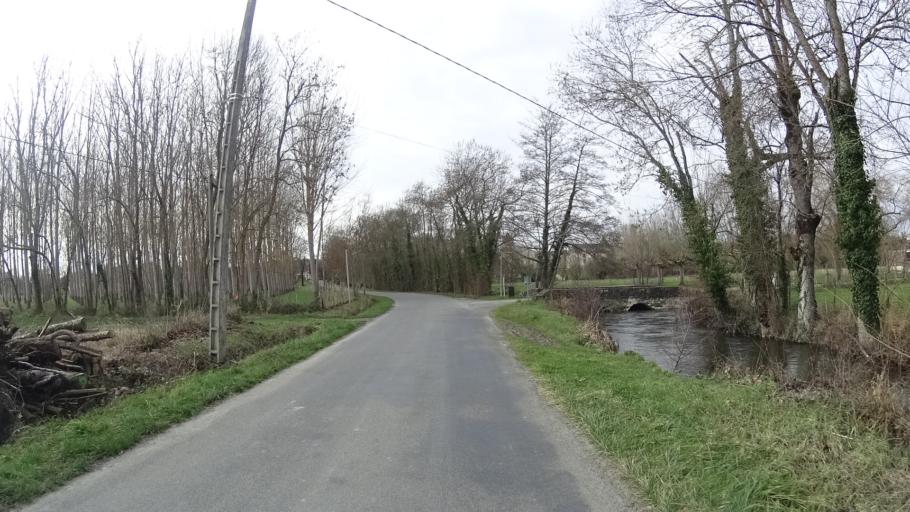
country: FR
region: Aquitaine
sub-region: Departement de la Dordogne
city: Saint-Aulaye
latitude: 45.2390
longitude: 0.1548
